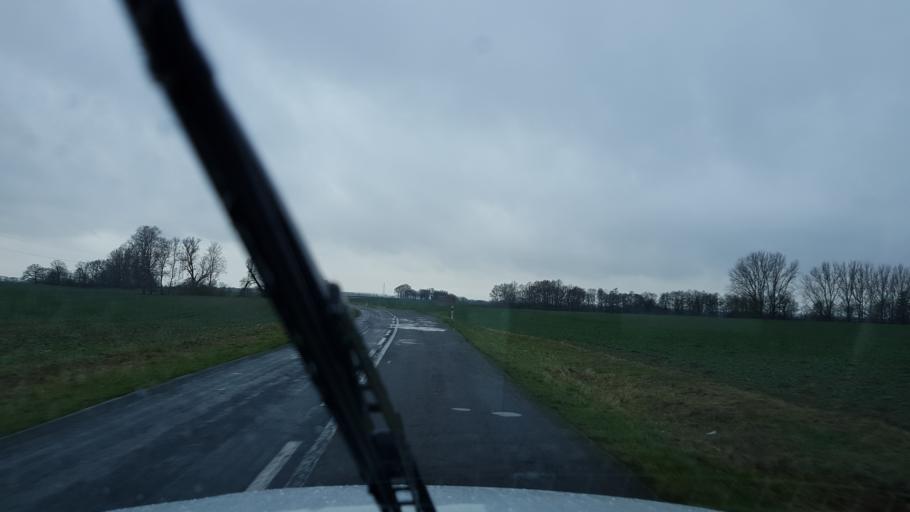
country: PL
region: West Pomeranian Voivodeship
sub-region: Powiat lobeski
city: Radowo Male
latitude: 53.6006
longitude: 15.4247
